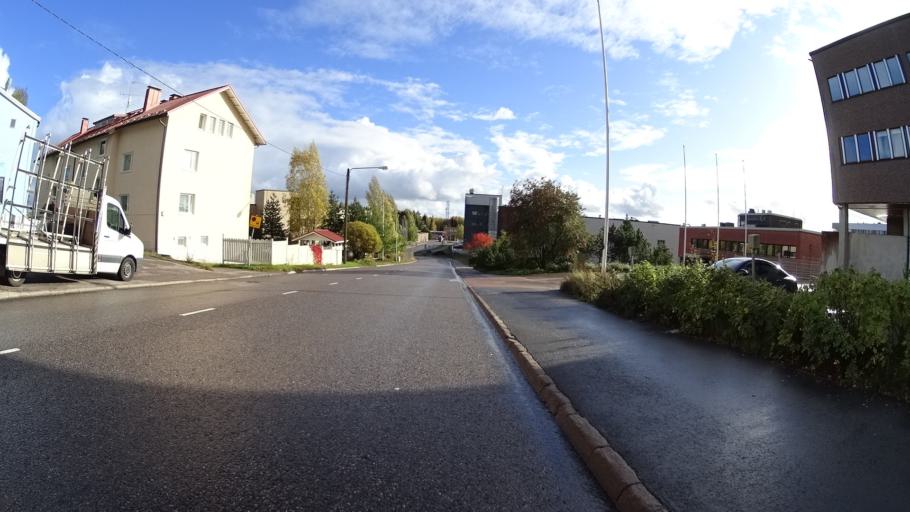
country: FI
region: Uusimaa
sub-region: Helsinki
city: Kilo
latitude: 60.2844
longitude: 24.8161
